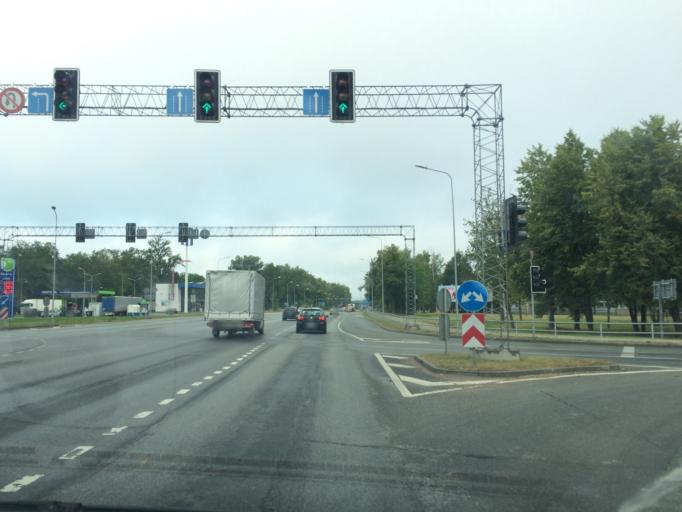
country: LV
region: Salaspils
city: Salaspils
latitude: 56.8514
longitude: 24.3363
